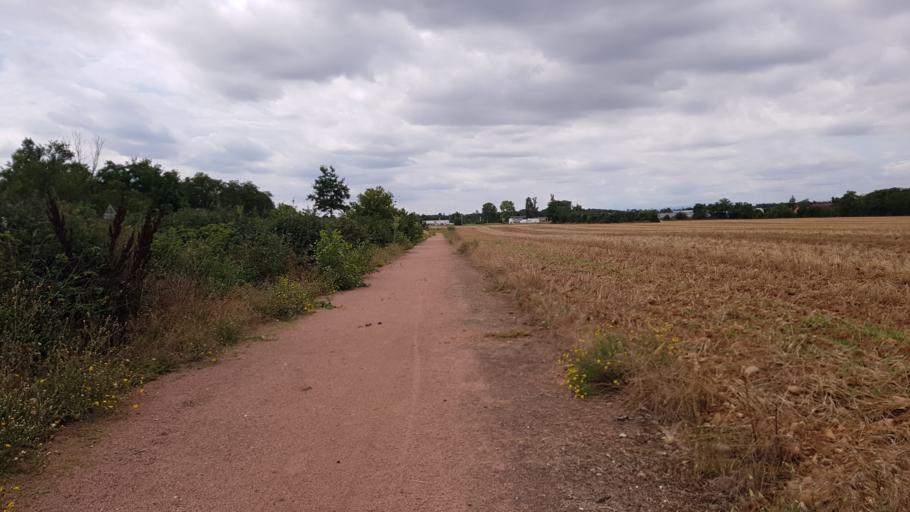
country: FR
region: Rhone-Alpes
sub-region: Departement du Rhone
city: Chassieu
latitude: 45.7223
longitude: 4.9558
